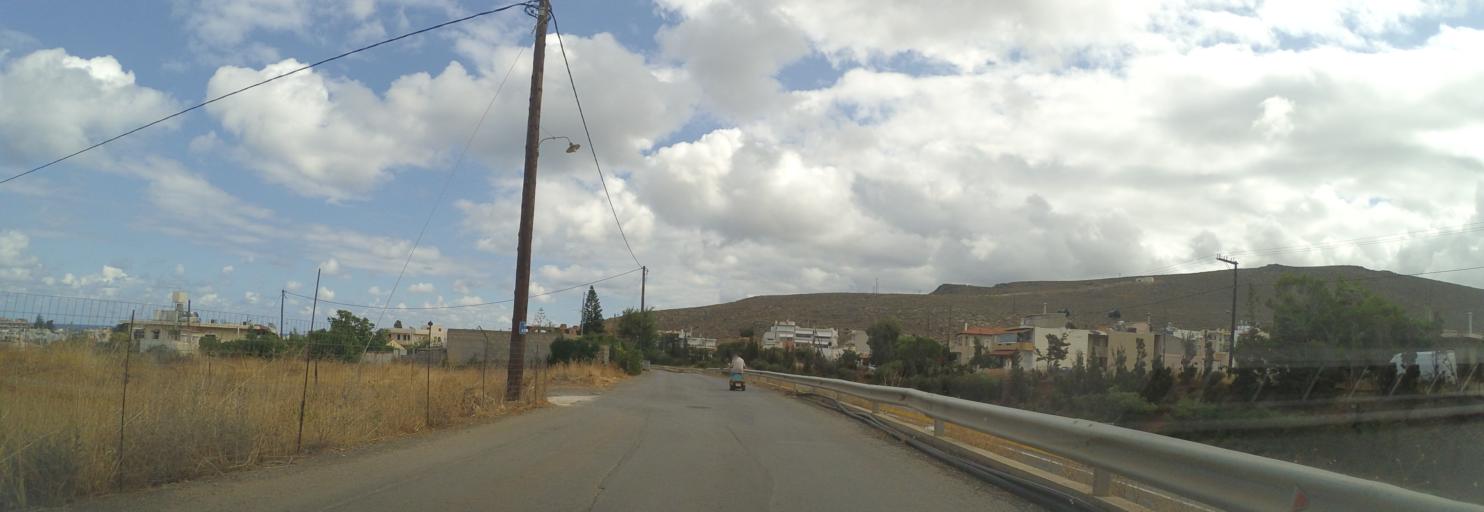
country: GR
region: Crete
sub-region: Nomos Irakleiou
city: Kokkini Hani
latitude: 35.3257
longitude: 25.2591
